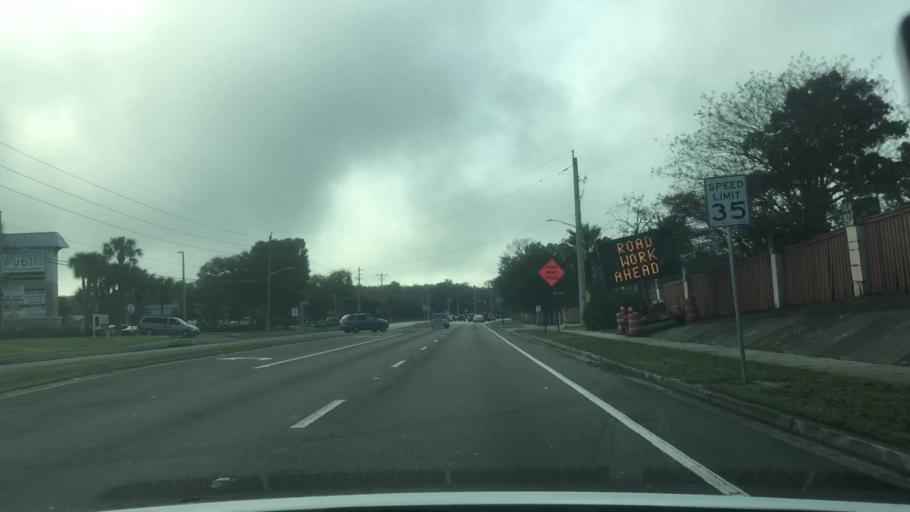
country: US
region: Florida
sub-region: Duval County
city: Atlantic Beach
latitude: 30.3628
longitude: -81.5029
